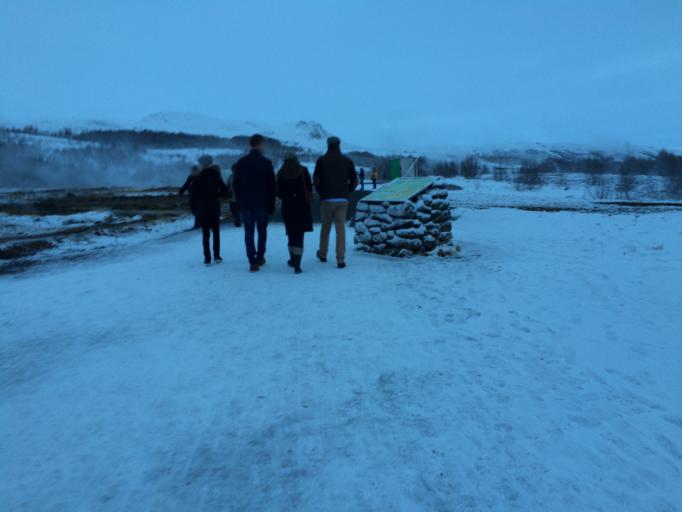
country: IS
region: South
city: Selfoss
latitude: 64.3104
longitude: -20.3014
